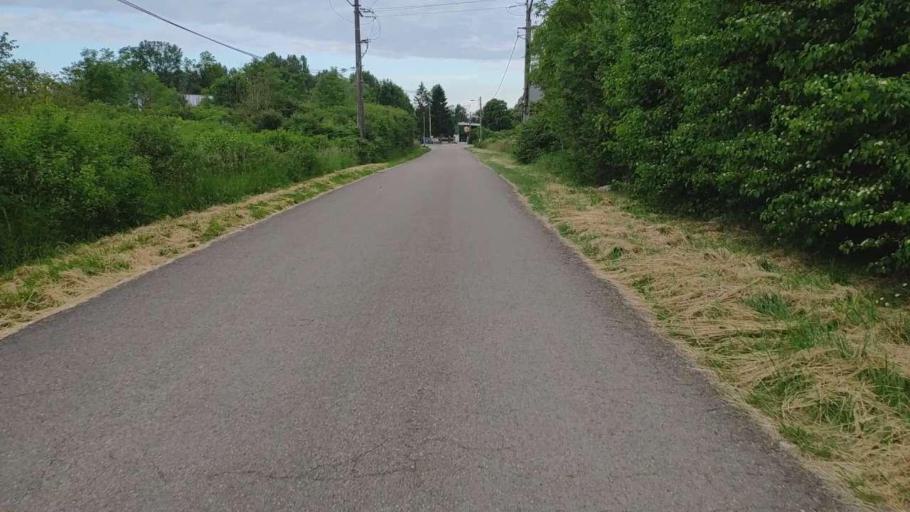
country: FR
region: Franche-Comte
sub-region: Departement du Jura
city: Bletterans
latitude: 46.7502
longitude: 5.4664
